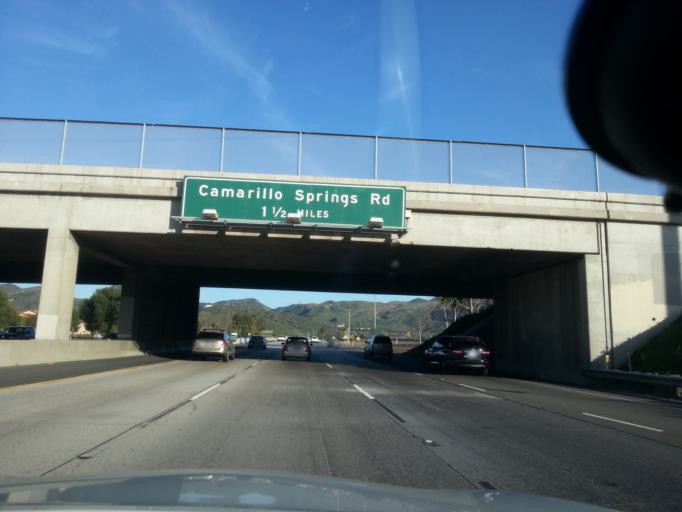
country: US
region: California
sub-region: Ventura County
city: Camarillo
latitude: 34.2138
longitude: -119.0083
